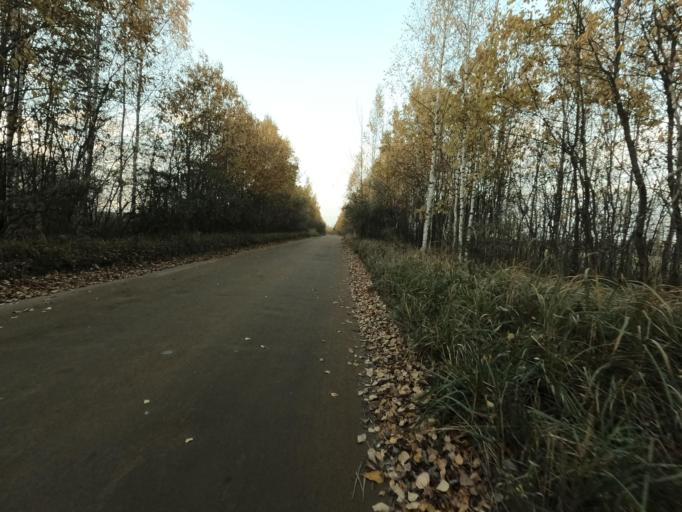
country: RU
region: Leningrad
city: Mga
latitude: 59.7939
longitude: 31.2007
